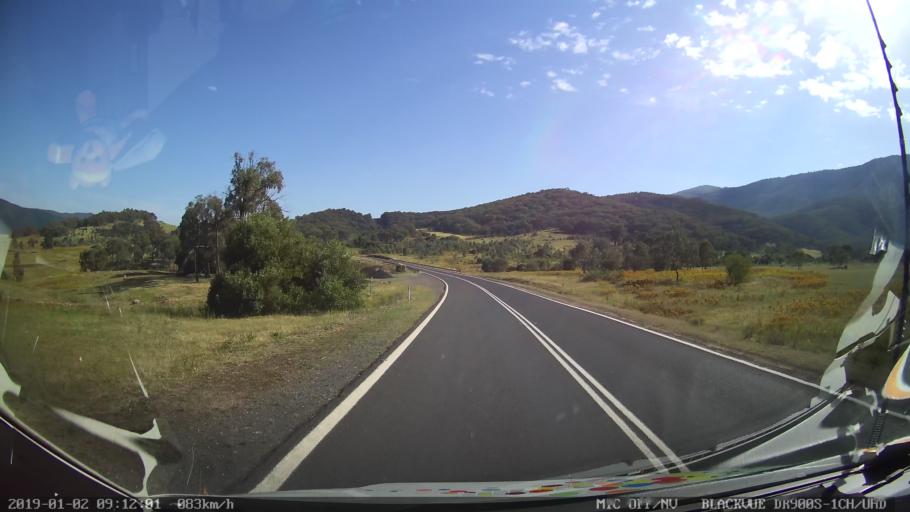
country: AU
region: New South Wales
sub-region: Tumut Shire
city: Tumut
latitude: -35.5056
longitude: 148.2720
